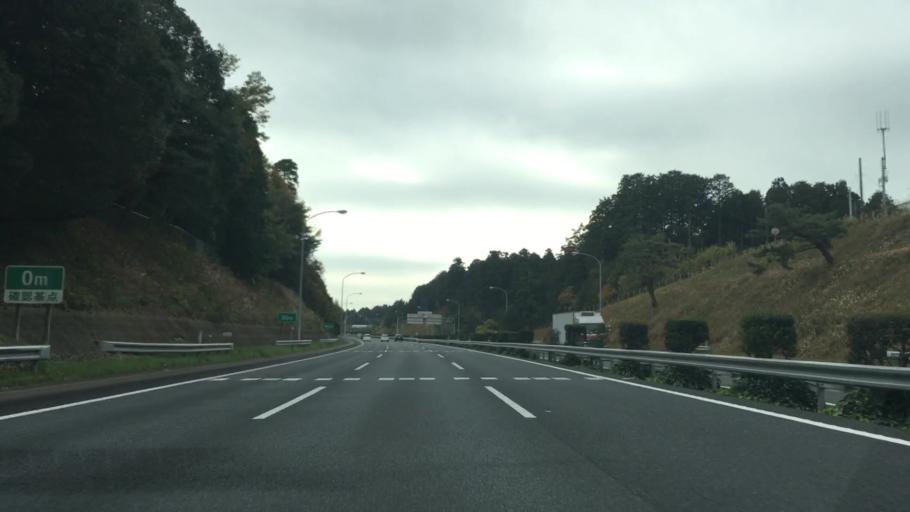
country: JP
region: Chiba
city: Narita
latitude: 35.7619
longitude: 140.3232
